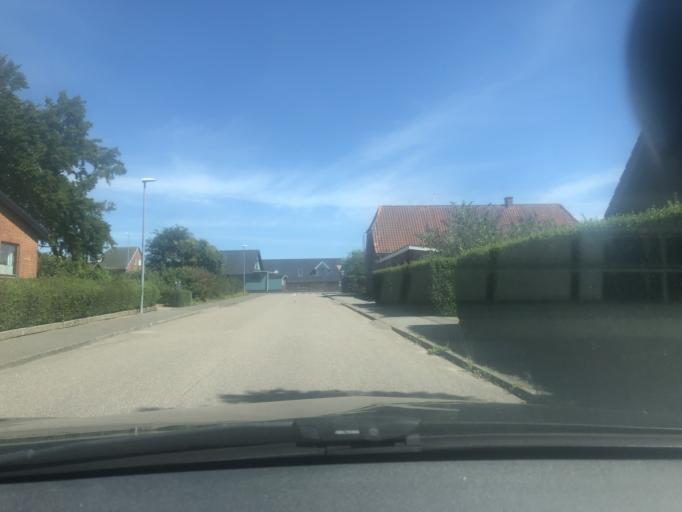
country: DK
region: South Denmark
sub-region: Vejle Kommune
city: Jelling
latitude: 55.7007
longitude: 9.3810
